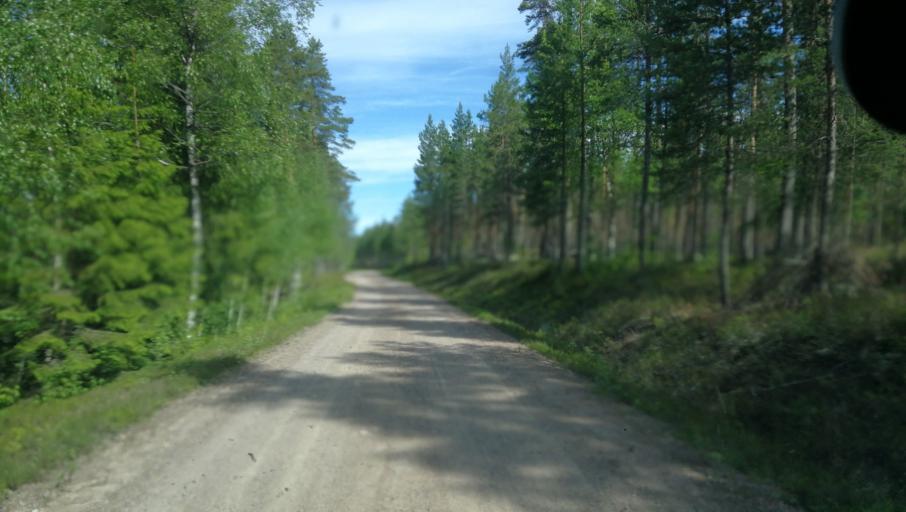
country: SE
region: Dalarna
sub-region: Vansbro Kommun
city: Vansbro
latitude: 60.8360
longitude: 14.1511
